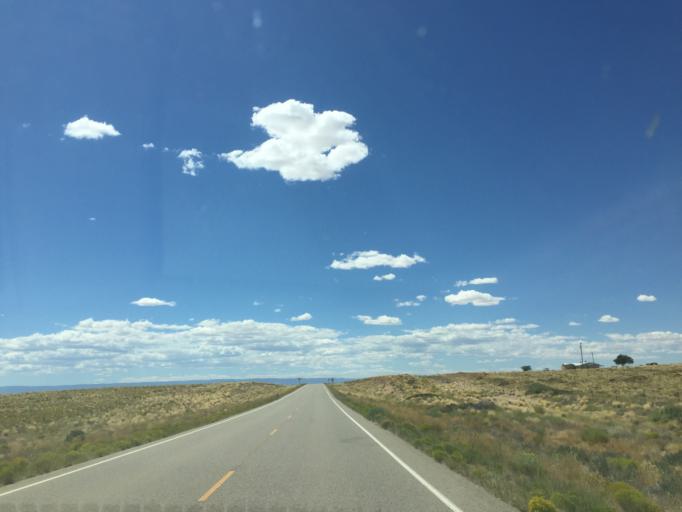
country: US
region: New Mexico
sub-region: San Juan County
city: Upper Fruitland
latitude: 36.4276
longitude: -108.3921
